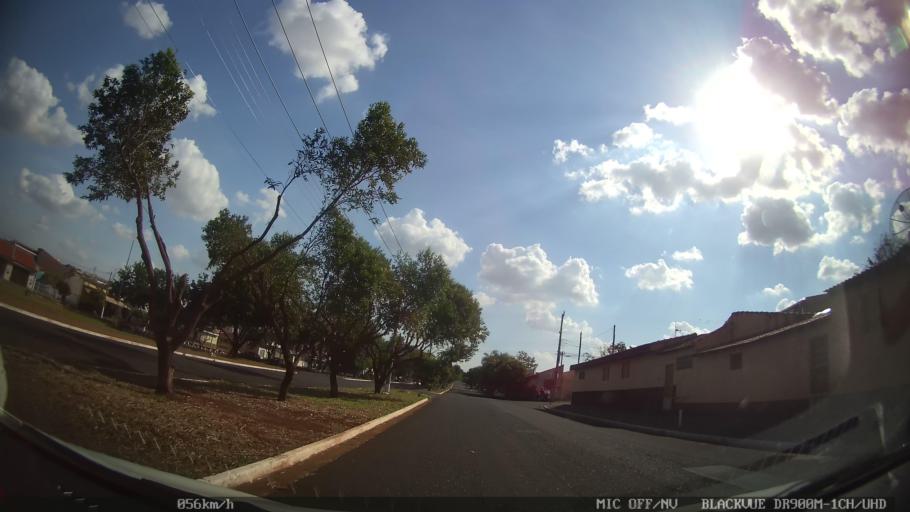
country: BR
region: Sao Paulo
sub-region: Ribeirao Preto
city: Ribeirao Preto
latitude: -21.1971
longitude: -47.8337
